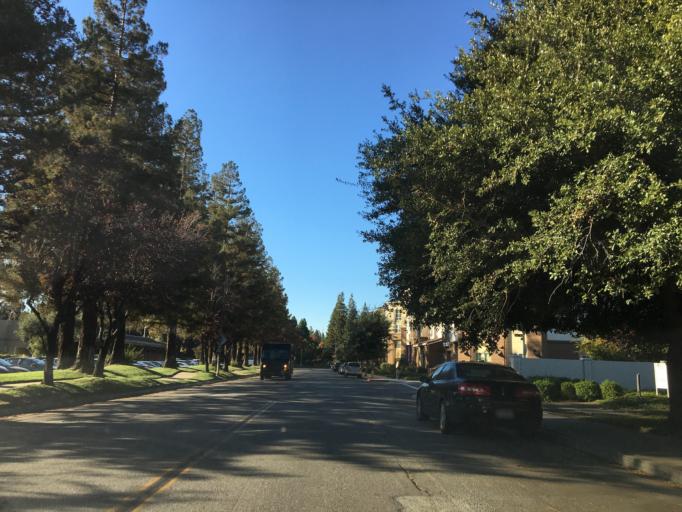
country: US
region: California
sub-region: Santa Clara County
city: Milpitas
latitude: 37.3978
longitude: -121.9204
